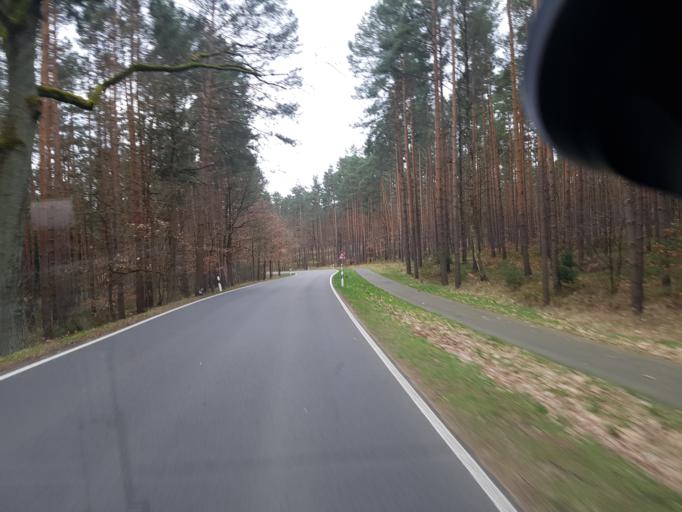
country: DE
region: Brandenburg
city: Gross Lindow
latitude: 52.1621
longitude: 14.5037
